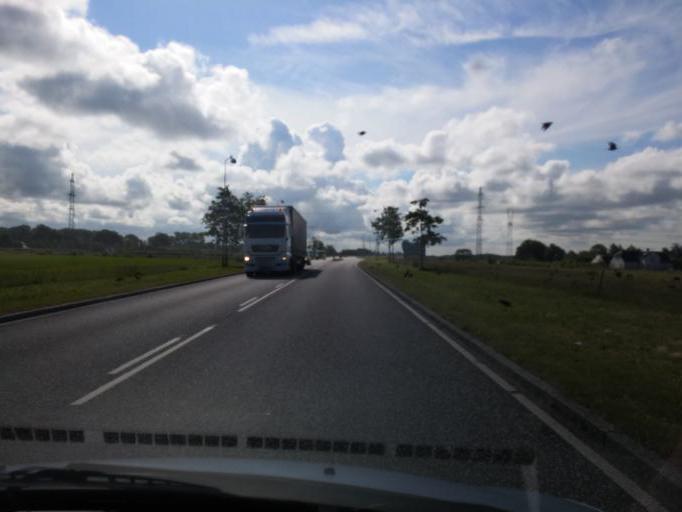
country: DK
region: South Denmark
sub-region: Odense Kommune
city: Neder Holluf
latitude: 55.3716
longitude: 10.5042
